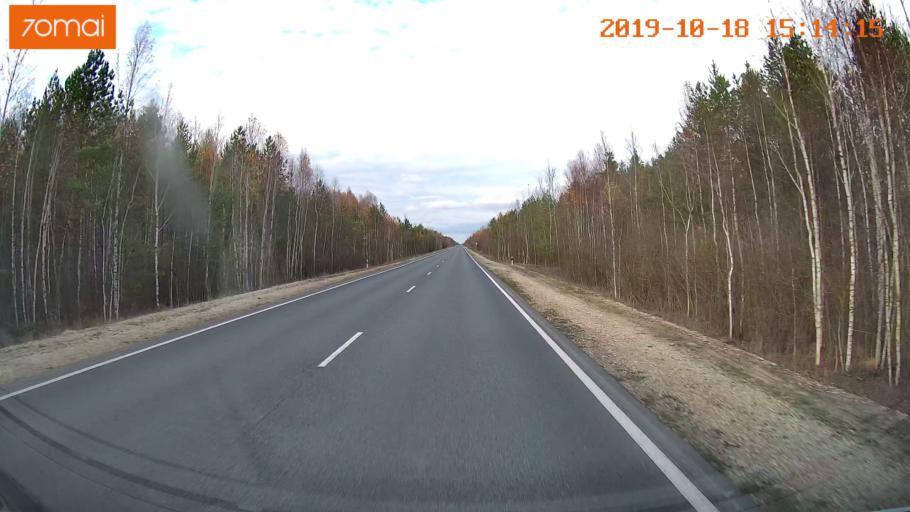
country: RU
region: Vladimir
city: Gus'-Khrustal'nyy
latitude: 55.5995
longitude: 40.7198
